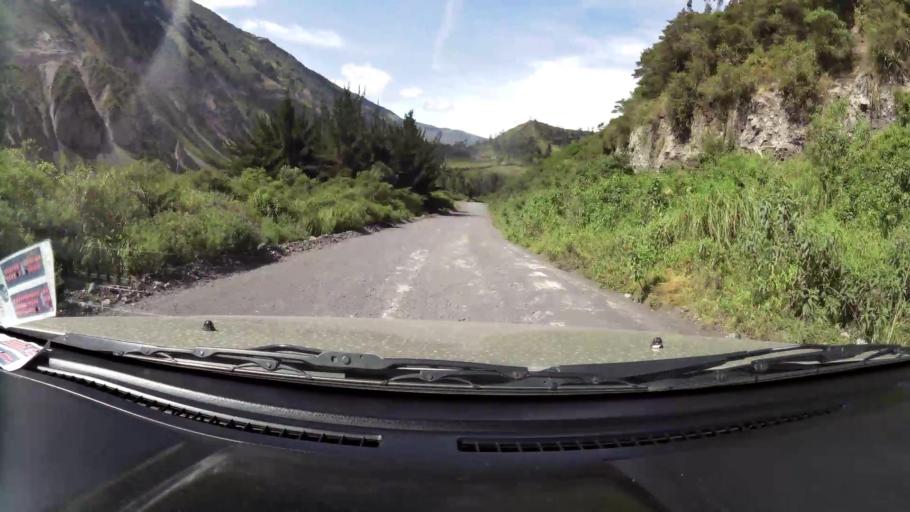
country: EC
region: Tungurahua
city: Banos
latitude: -1.4925
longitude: -78.5120
